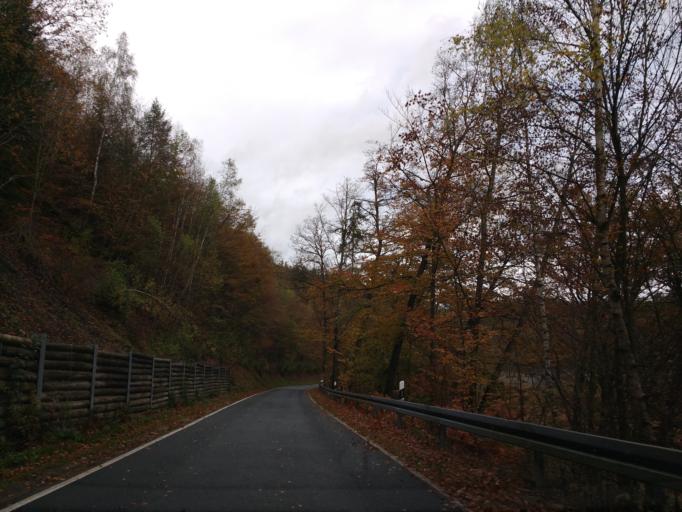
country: DE
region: Hesse
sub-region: Regierungsbezirk Kassel
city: Vohl
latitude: 51.1813
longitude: 8.9448
